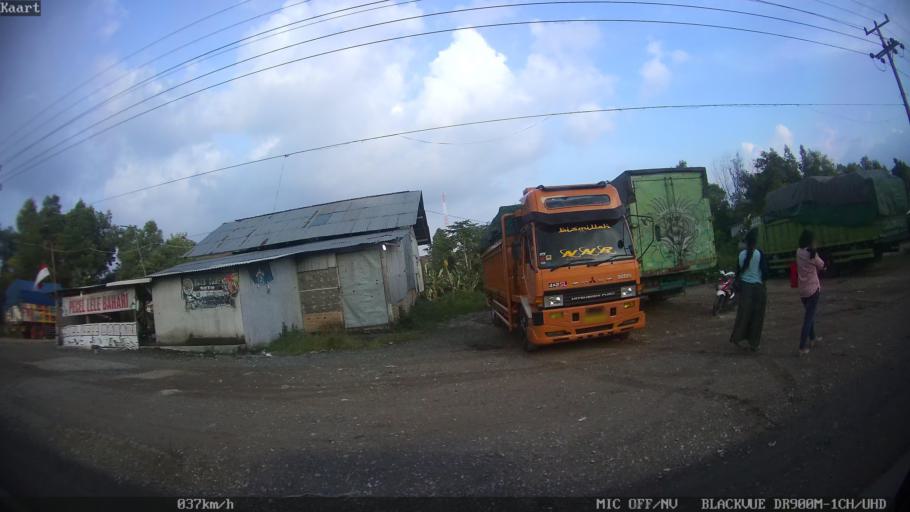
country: ID
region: Lampung
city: Panjang
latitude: -5.4144
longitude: 105.3456
